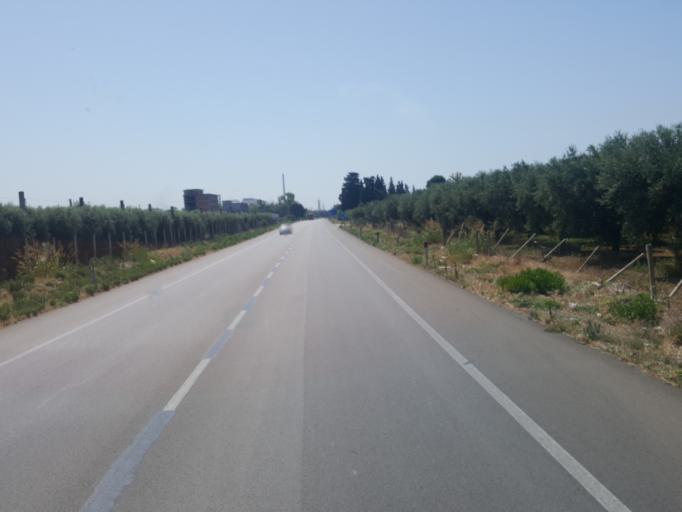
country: IT
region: Apulia
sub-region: Provincia di Taranto
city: Statte
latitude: 40.5212
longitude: 17.1784
